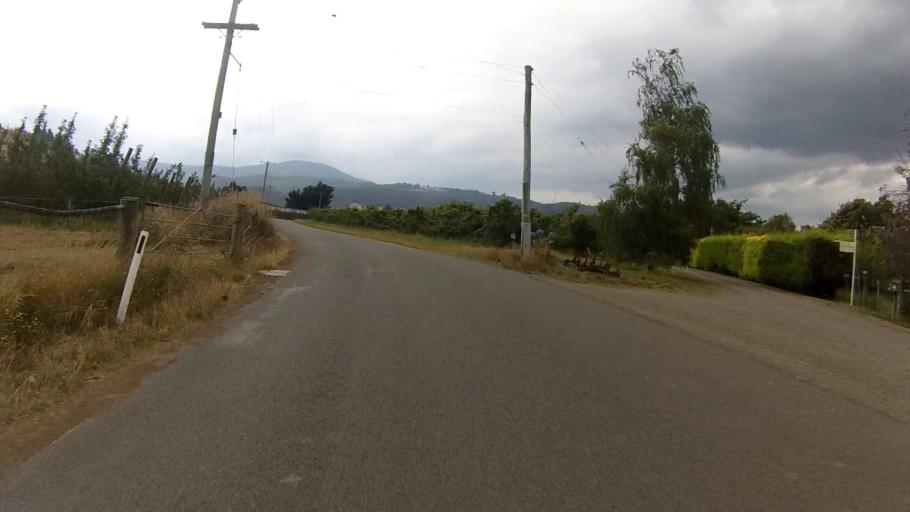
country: AU
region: Tasmania
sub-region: Huon Valley
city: Huonville
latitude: -42.9918
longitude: 147.0627
